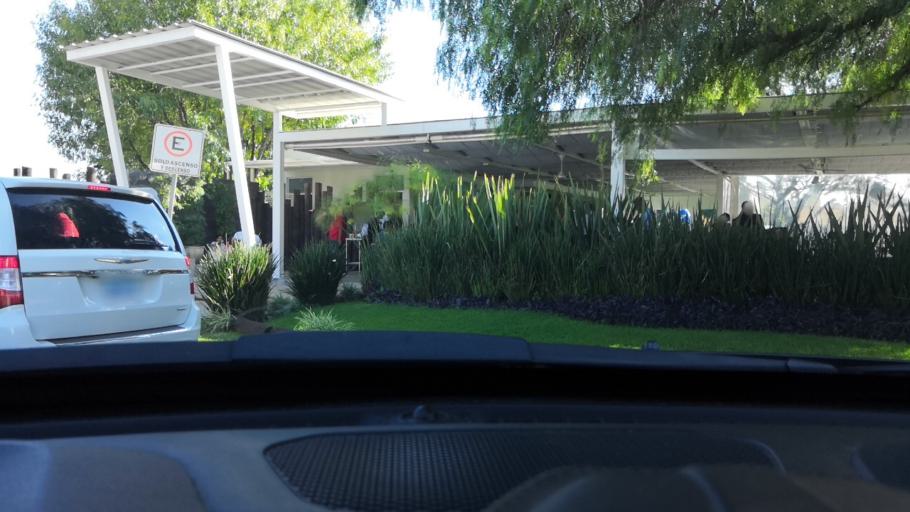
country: MX
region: Guanajuato
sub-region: Leon
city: Medina
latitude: 21.1668
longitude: -101.6418
